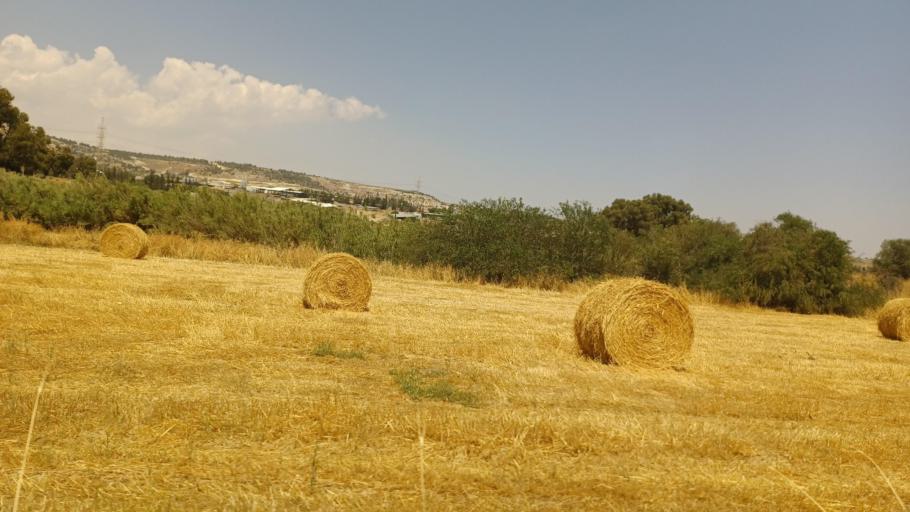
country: CY
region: Larnaka
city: Voroklini
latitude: 35.0006
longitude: 33.6505
